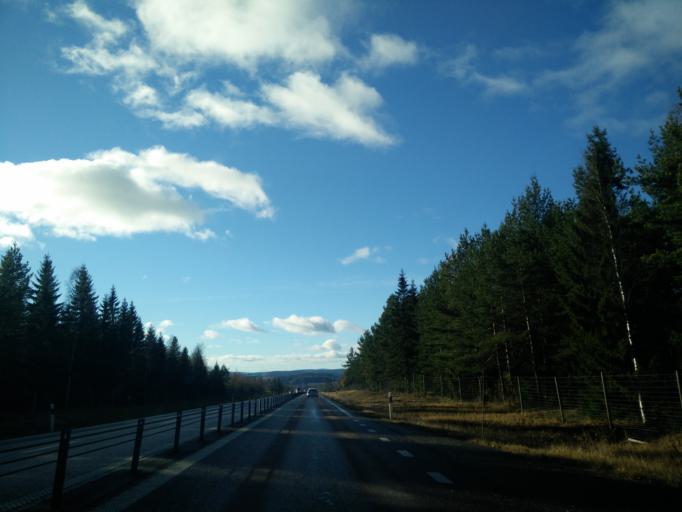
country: SE
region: Vaesternorrland
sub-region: Timra Kommun
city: Soraker
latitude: 62.5323
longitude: 17.5010
